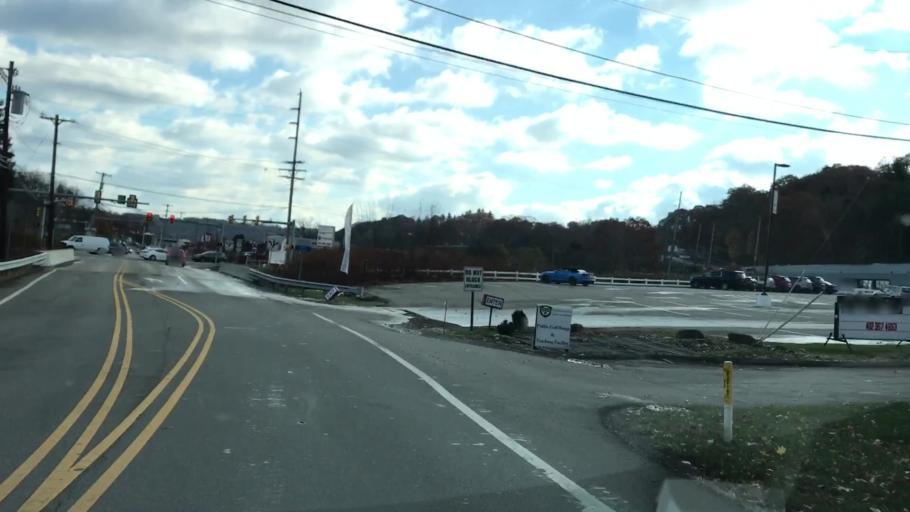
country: US
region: Pennsylvania
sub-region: Allegheny County
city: Franklin Park
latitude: 40.5868
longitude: -80.0464
